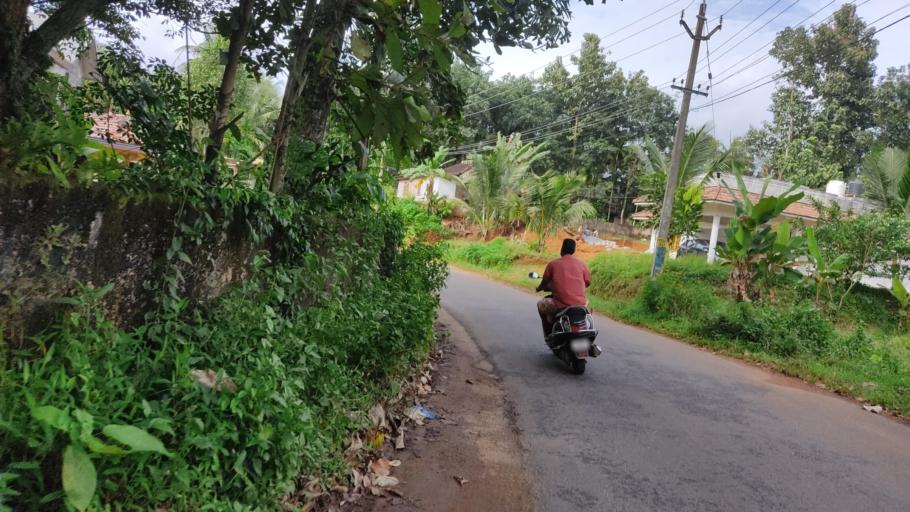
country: IN
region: Kerala
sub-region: Pattanamtitta
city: Adur
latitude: 9.1984
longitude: 76.7787
